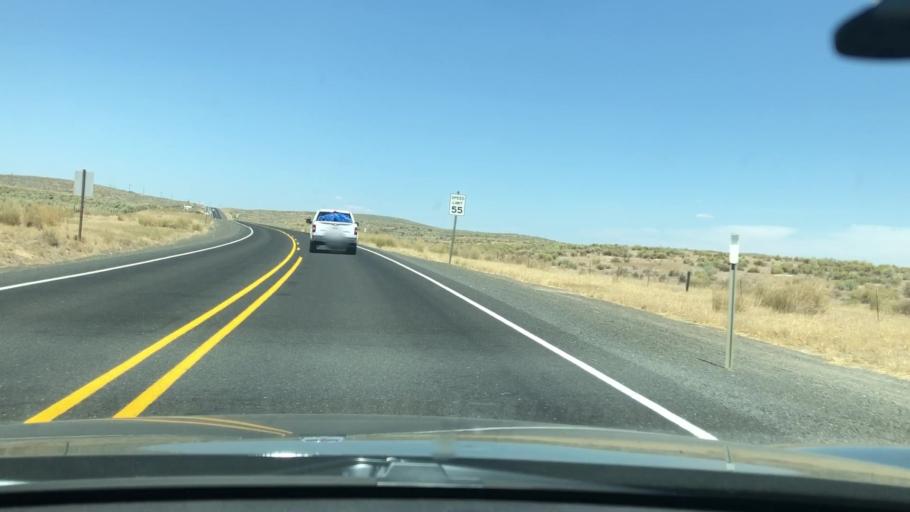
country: US
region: Idaho
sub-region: Owyhee County
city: Murphy
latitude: 42.9836
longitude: -117.0535
